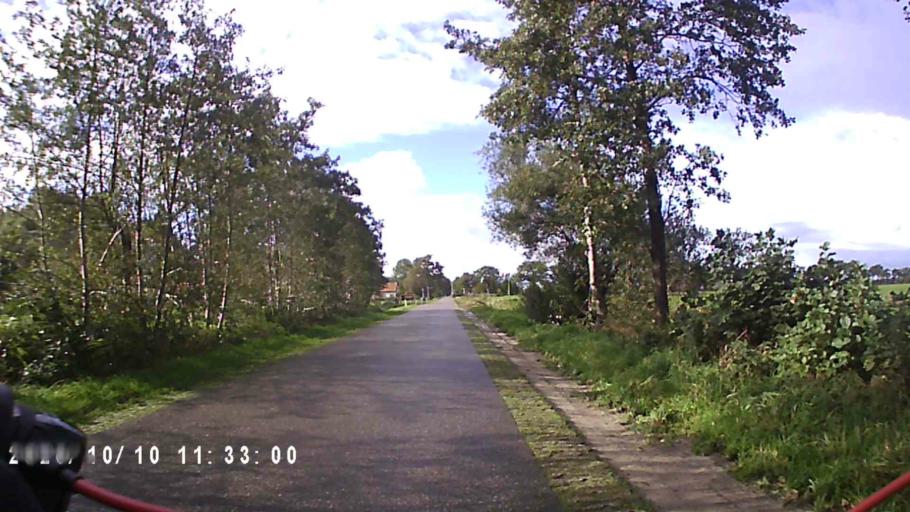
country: NL
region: Friesland
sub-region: Gemeente Smallingerland
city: Drachten
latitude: 53.0814
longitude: 6.1319
